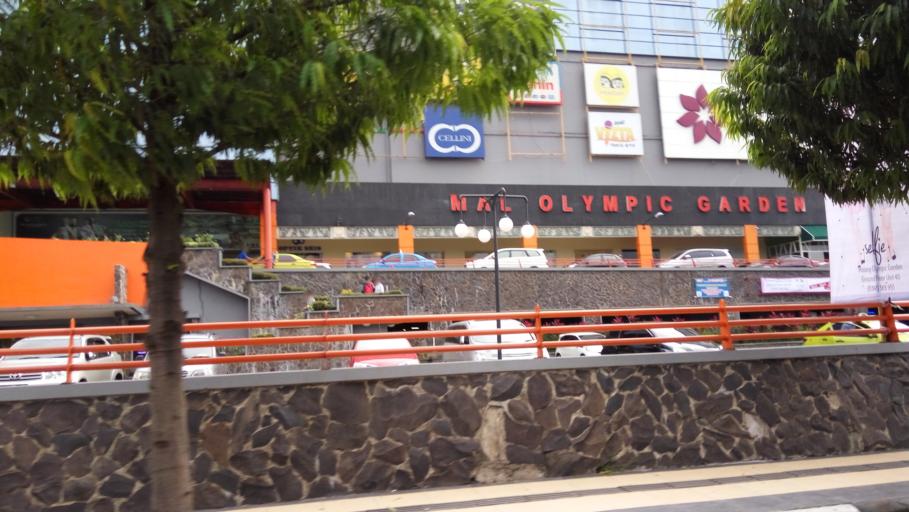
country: ID
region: East Java
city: Malang
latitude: -7.9775
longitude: 112.6234
